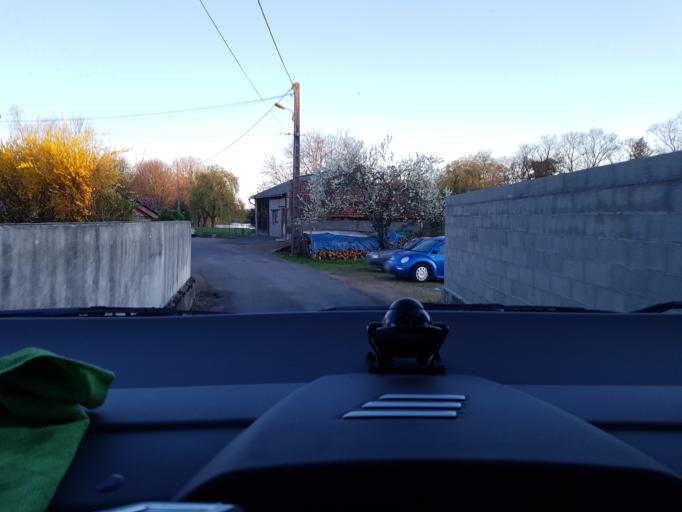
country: FR
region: Bourgogne
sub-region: Departement de Saone-et-Loire
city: Etang-sur-Arroux
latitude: 46.8659
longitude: 4.1885
